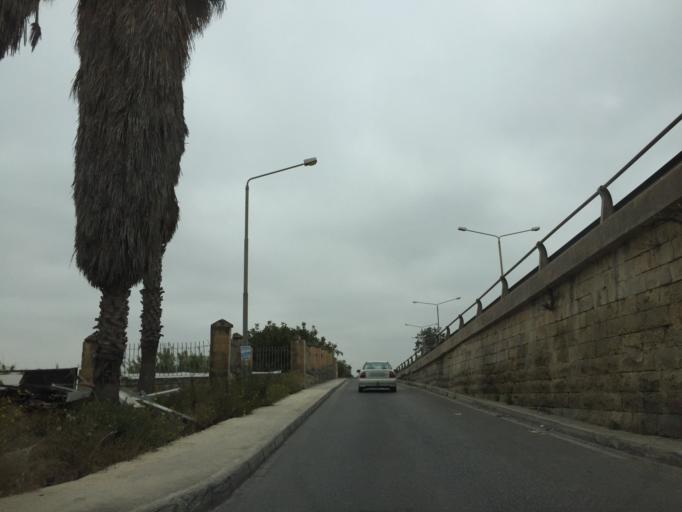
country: MT
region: Saint Venera
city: Santa Venera
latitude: 35.8840
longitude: 14.4726
